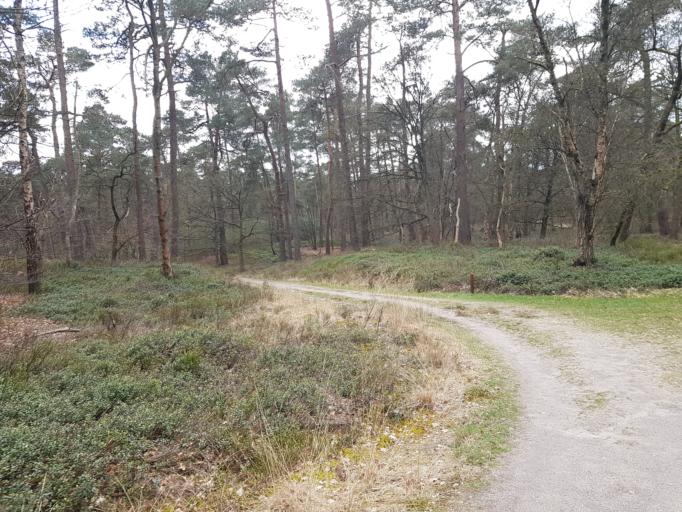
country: NL
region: Gelderland
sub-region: Gemeente Apeldoorn
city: Apeldoorn
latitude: 52.2362
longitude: 5.9014
